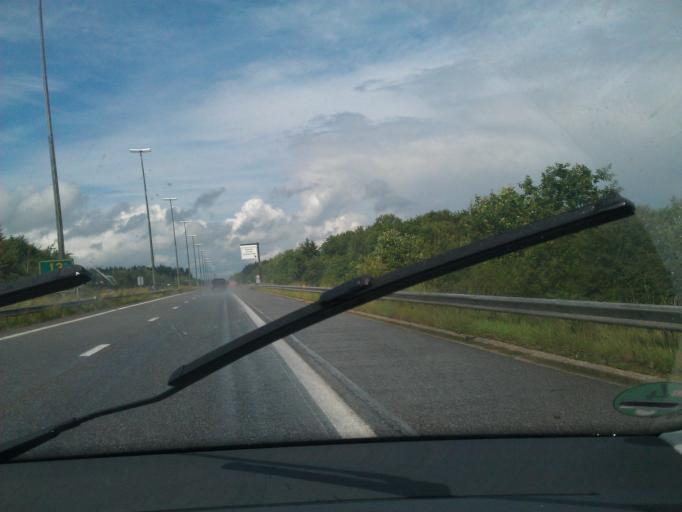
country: BE
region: Wallonia
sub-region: Province de Liege
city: Saint-Vith
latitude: 50.3119
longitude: 6.0823
